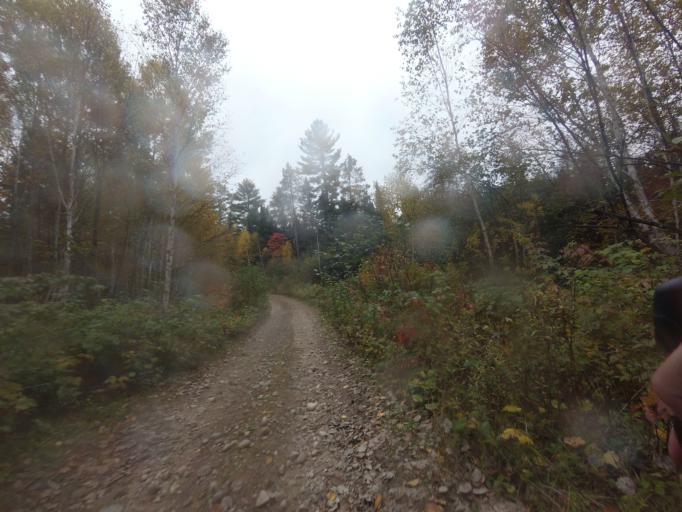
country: CA
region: Ontario
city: Petawawa
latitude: 45.7798
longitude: -77.3831
